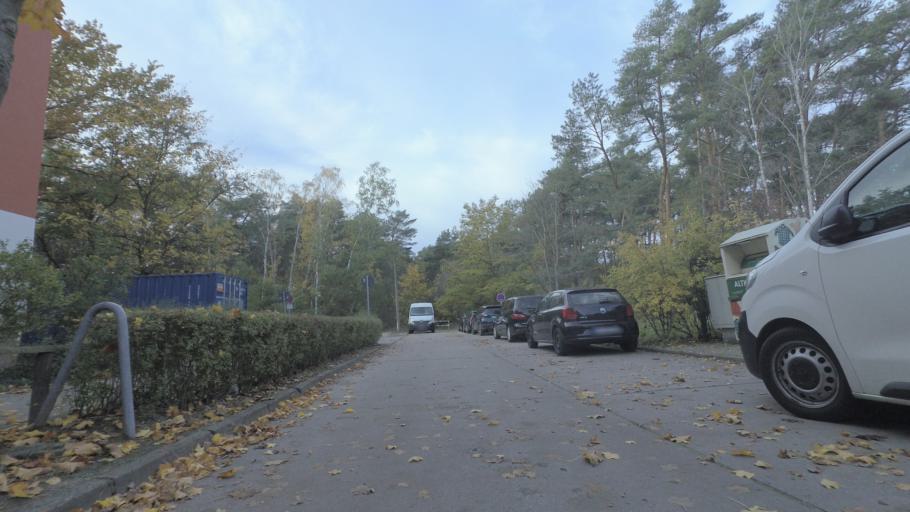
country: DE
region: Brandenburg
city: Ludwigsfelde
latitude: 52.3052
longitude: 13.2392
